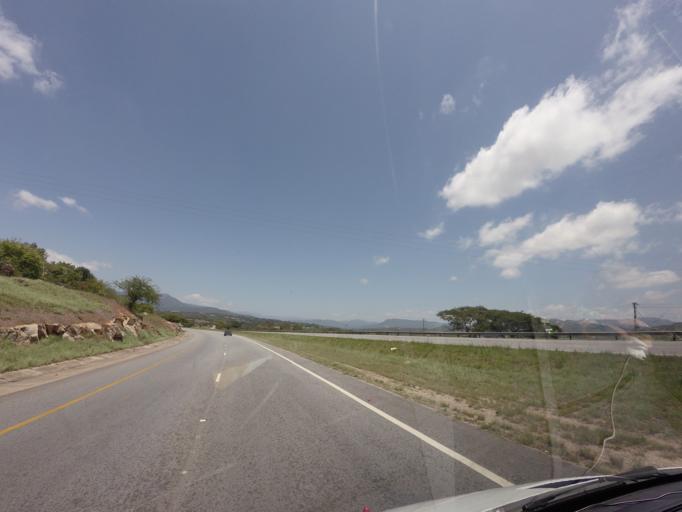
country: ZA
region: Mpumalanga
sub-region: Ehlanzeni District
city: Nelspruit
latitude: -25.4446
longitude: 30.8741
